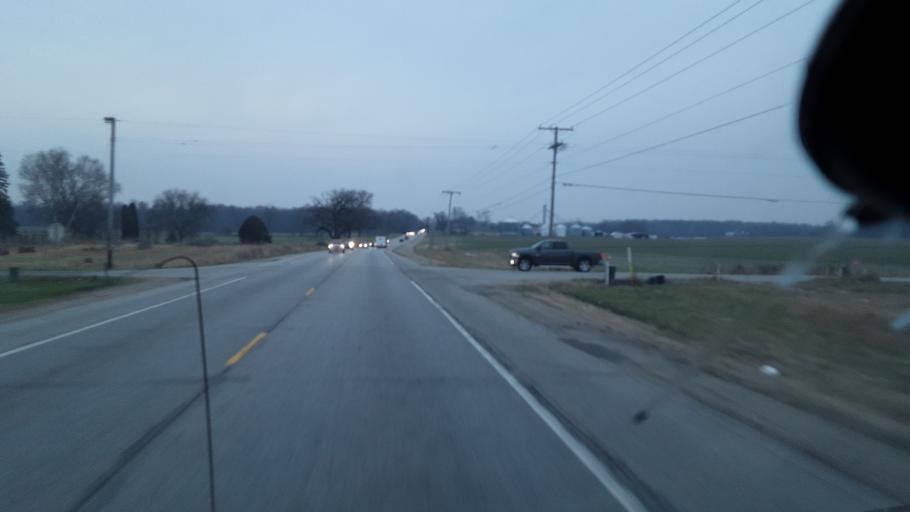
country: US
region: Indiana
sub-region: Elkhart County
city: Middlebury
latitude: 41.6677
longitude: -85.7722
